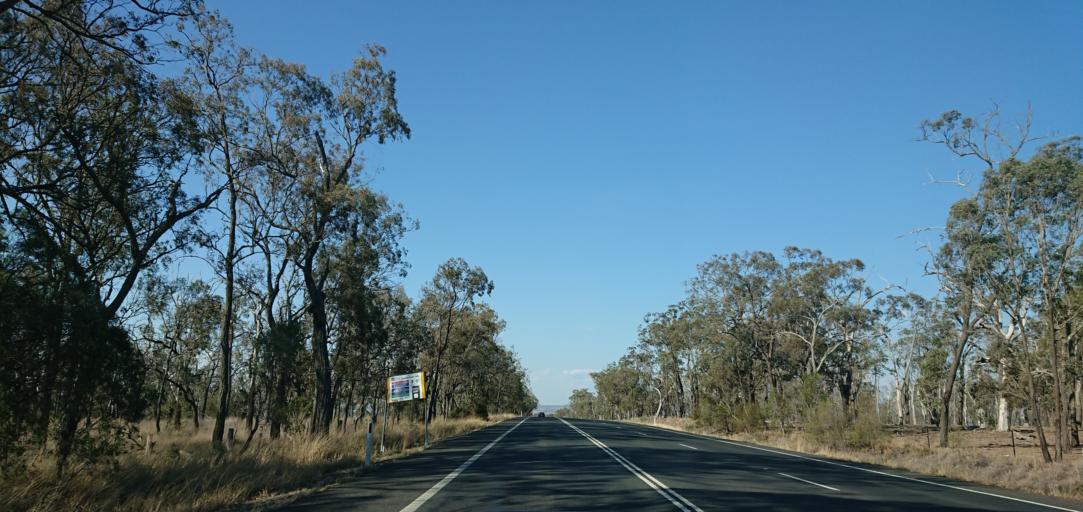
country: AU
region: Queensland
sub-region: Toowoomba
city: Westbrook
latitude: -27.6239
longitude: 151.7621
